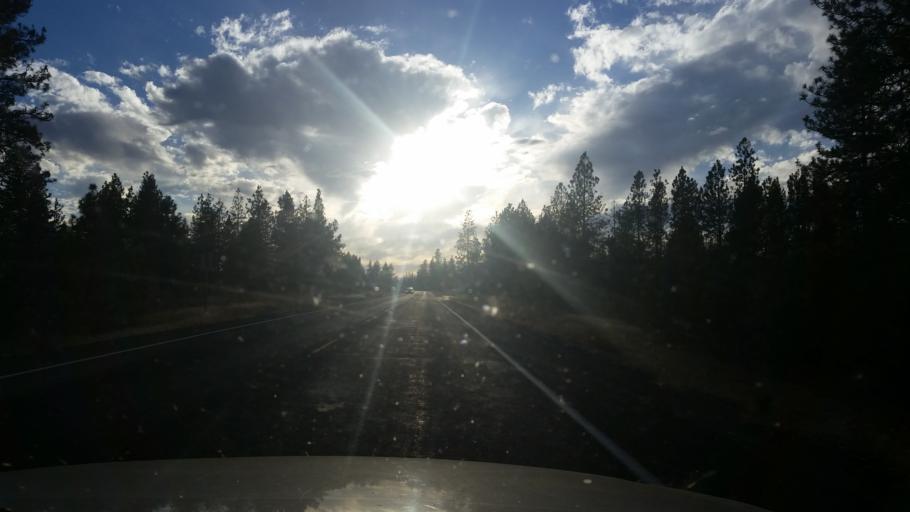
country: US
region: Washington
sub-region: Spokane County
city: Medical Lake
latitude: 47.4365
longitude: -117.7780
